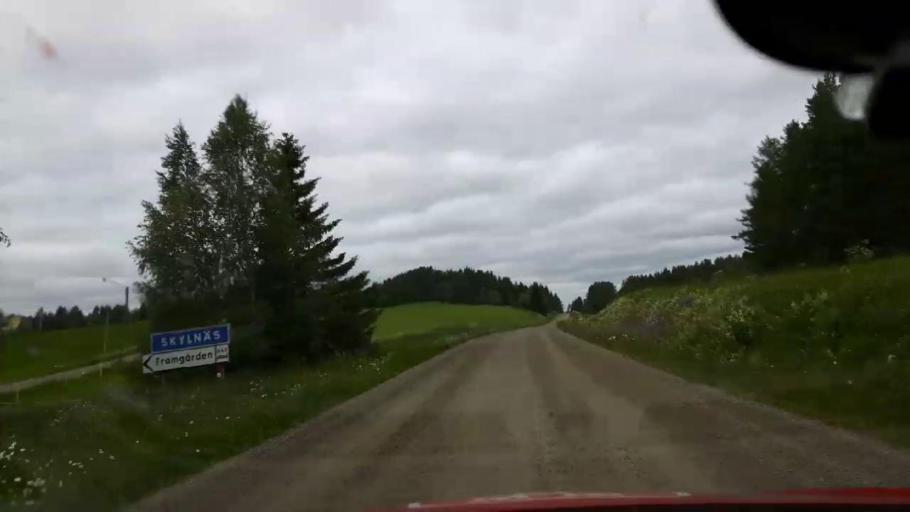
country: SE
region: Jaemtland
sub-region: OEstersunds Kommun
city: Brunflo
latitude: 62.9190
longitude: 15.0162
